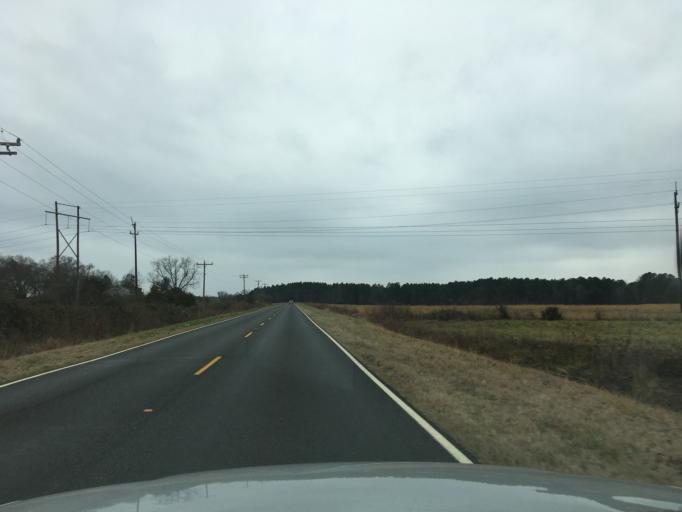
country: US
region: South Carolina
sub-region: Greenwood County
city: Greenwood
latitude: 34.1240
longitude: -82.1636
